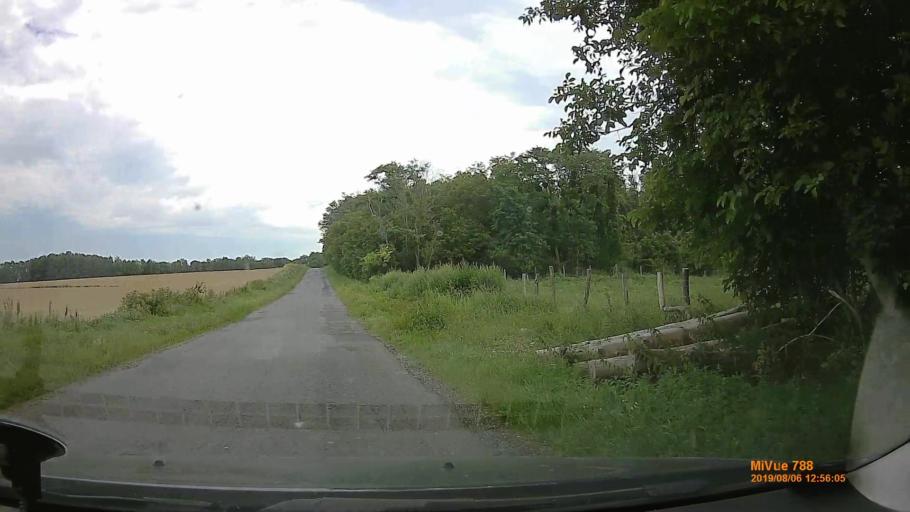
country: HU
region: Zala
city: Pacsa
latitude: 46.6350
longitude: 17.0258
